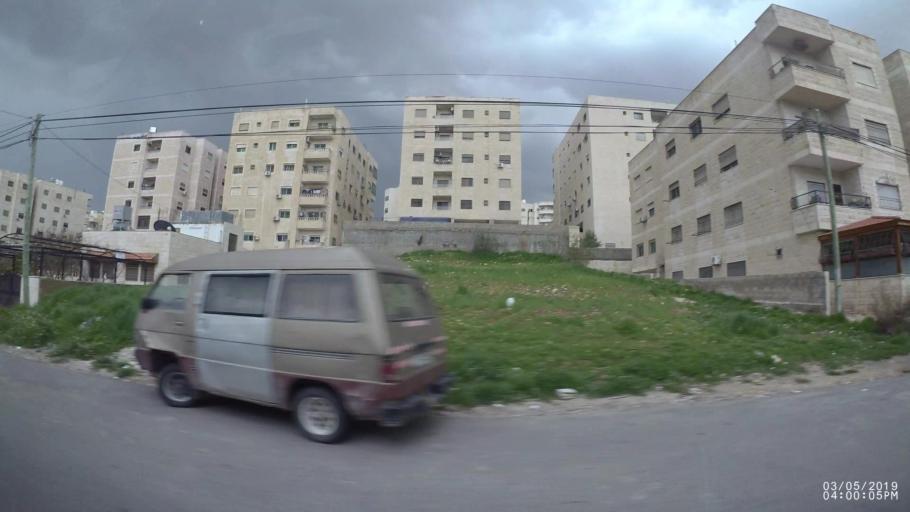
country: JO
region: Amman
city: Amman
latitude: 32.0103
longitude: 35.9587
